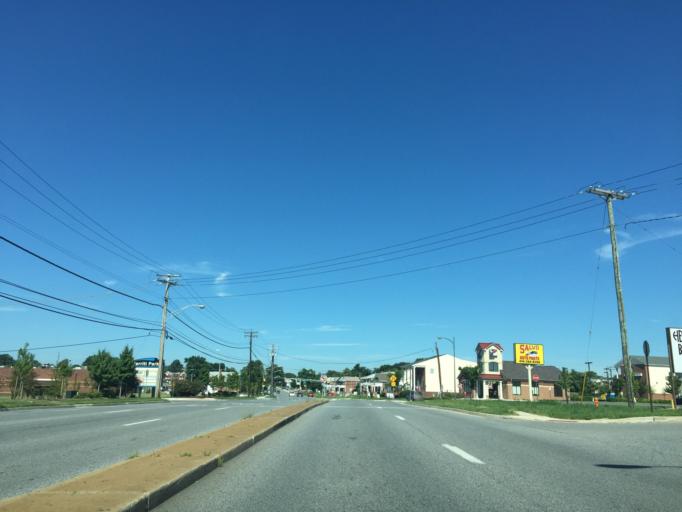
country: US
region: Maryland
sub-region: Baltimore County
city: Dundalk
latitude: 39.2702
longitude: -76.5039
